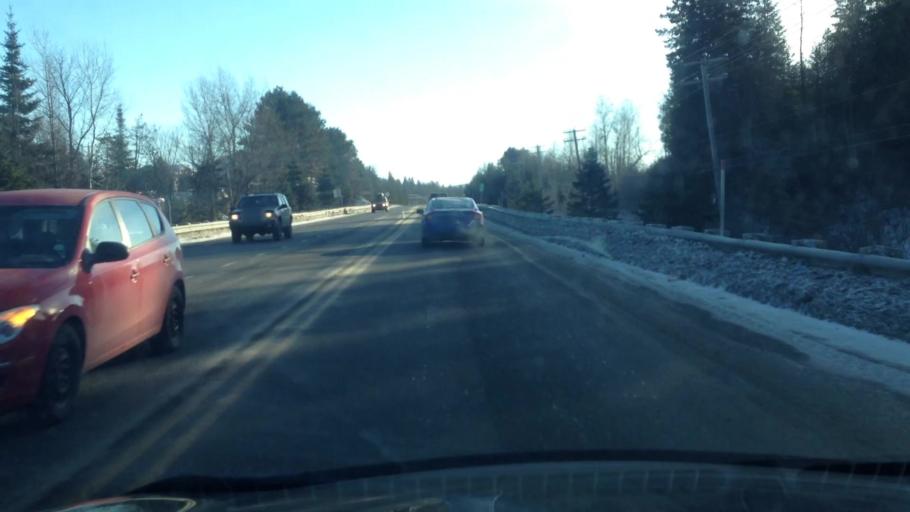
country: CA
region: Quebec
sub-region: Laurentides
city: Saint-Sauveur
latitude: 45.8956
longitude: -74.2030
